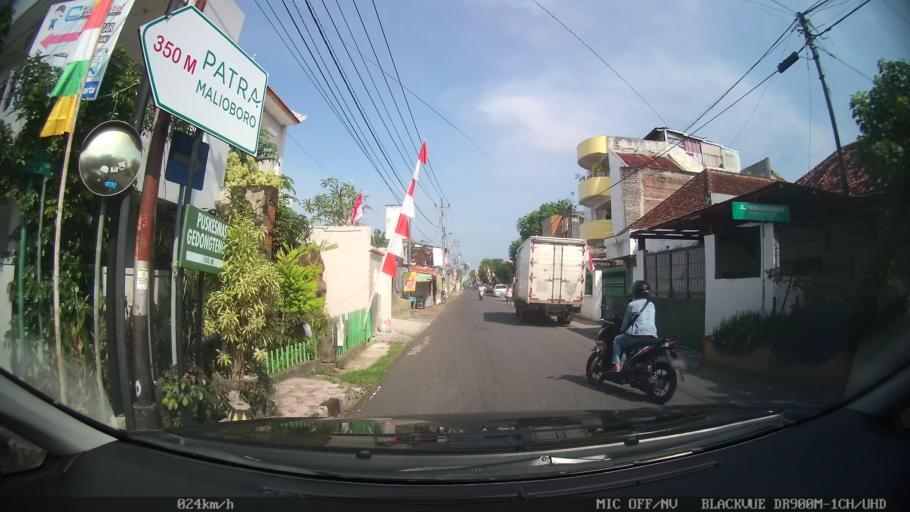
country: ID
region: Daerah Istimewa Yogyakarta
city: Yogyakarta
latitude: -7.7915
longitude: 110.3604
